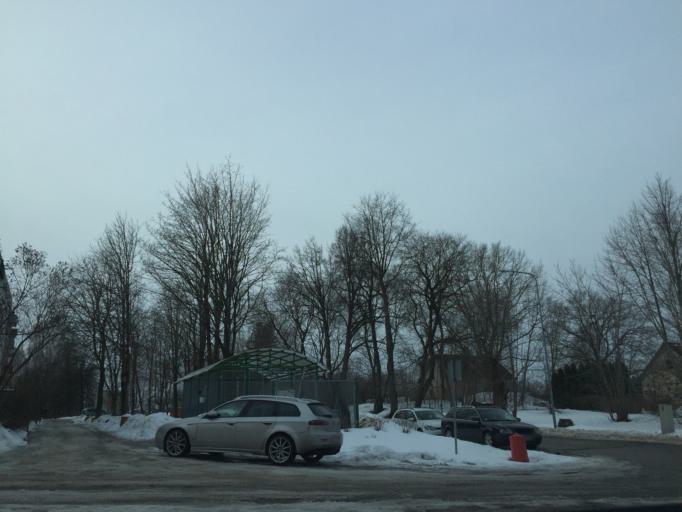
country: LV
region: Ikskile
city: Ikskile
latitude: 56.8458
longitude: 24.4408
